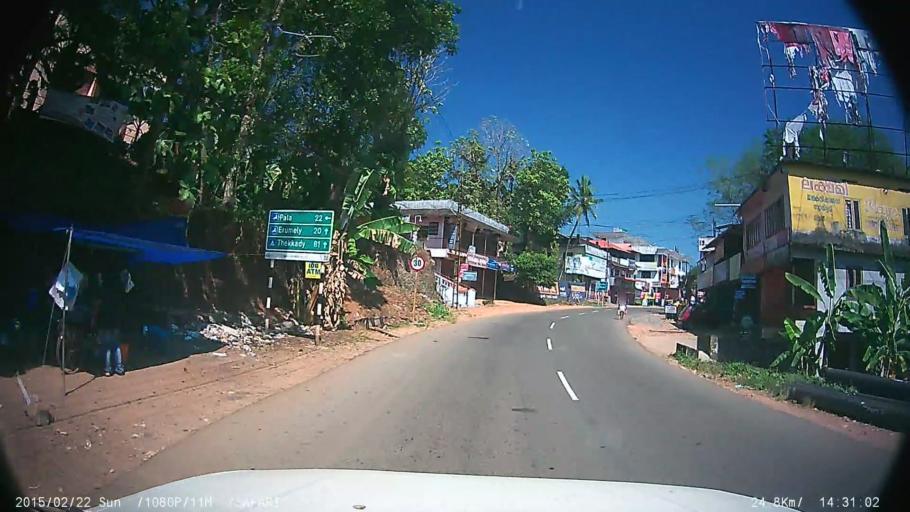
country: IN
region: Kerala
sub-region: Kottayam
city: Erattupetta
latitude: 9.5660
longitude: 76.7522
